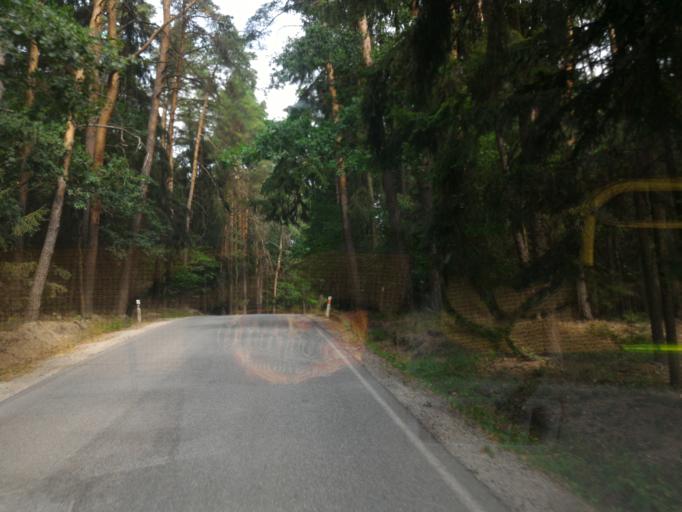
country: CZ
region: Jihocesky
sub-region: Okres Jindrichuv Hradec
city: Dacice
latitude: 49.0951
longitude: 15.4789
